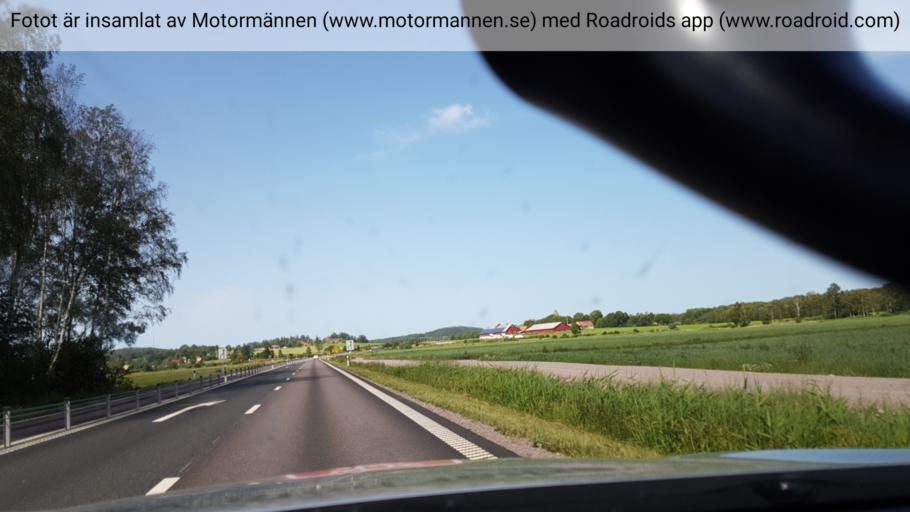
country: SE
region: Joenkoeping
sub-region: Tranas Kommun
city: Tranas
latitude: 57.9822
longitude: 14.9143
